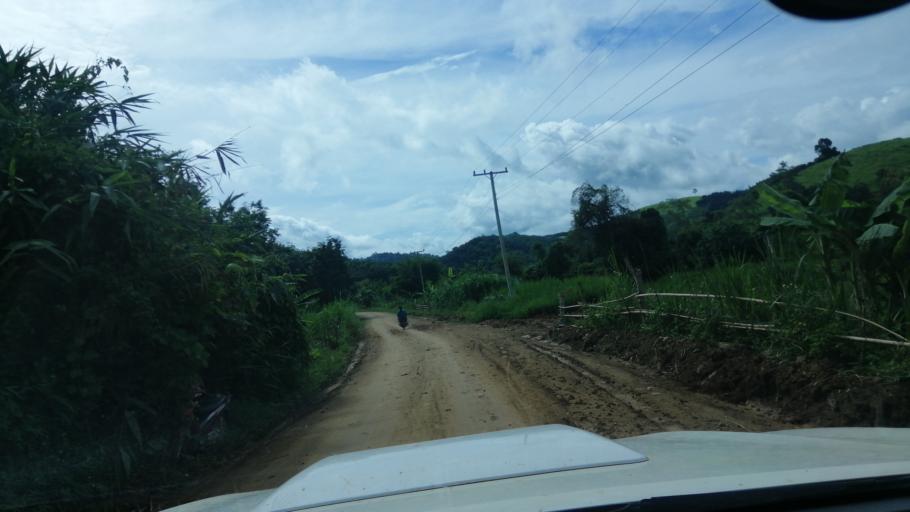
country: TH
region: Phayao
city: Phu Sang
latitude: 19.6354
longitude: 100.5277
